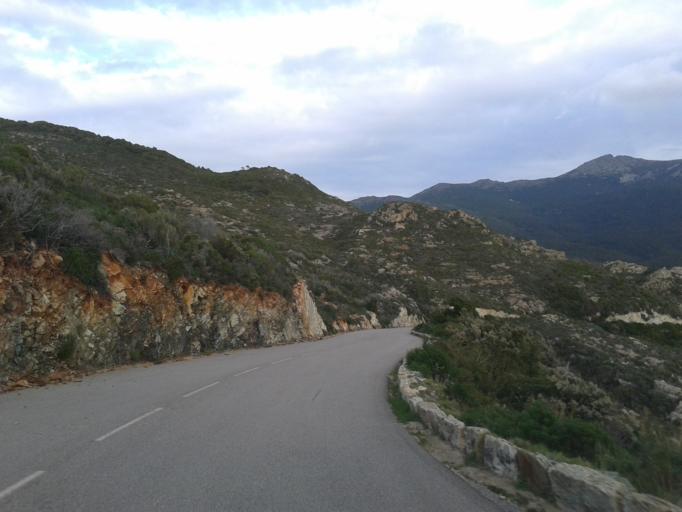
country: FR
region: Corsica
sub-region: Departement de la Haute-Corse
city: Brando
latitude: 42.8721
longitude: 9.3338
